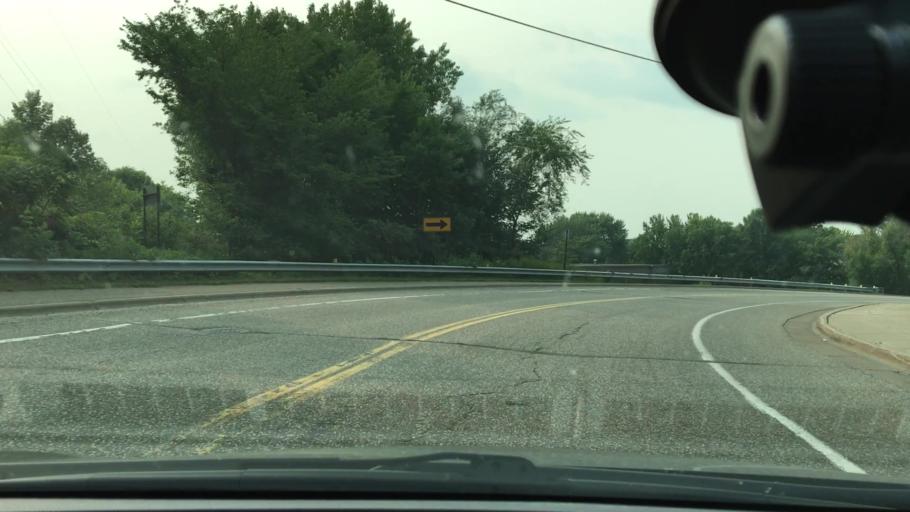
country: US
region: Minnesota
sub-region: Hennepin County
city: Dayton
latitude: 45.2421
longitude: -93.5150
